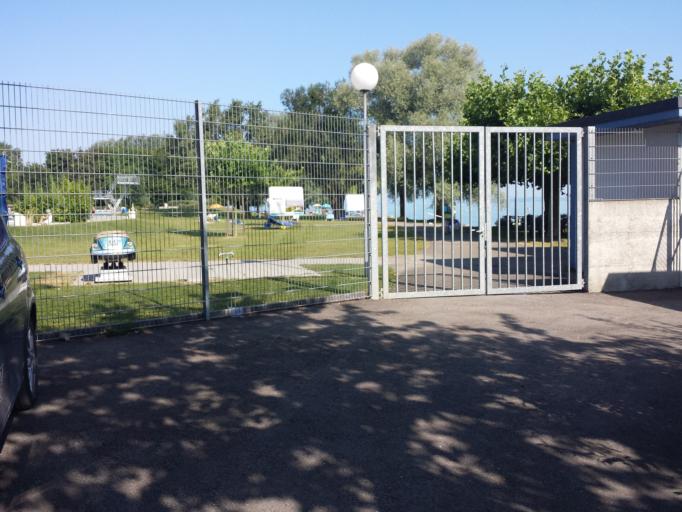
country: CH
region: Thurgau
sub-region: Arbon District
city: Romanshorn
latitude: 47.5733
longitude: 9.3772
